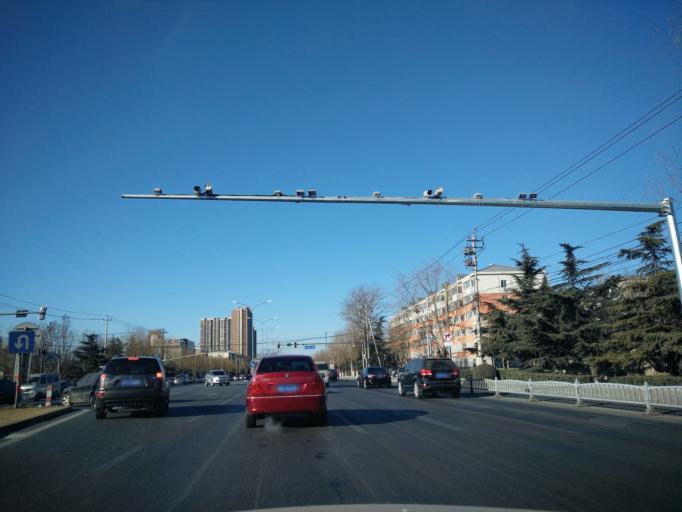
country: CN
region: Beijing
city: Xingfeng
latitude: 39.7205
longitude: 116.3481
